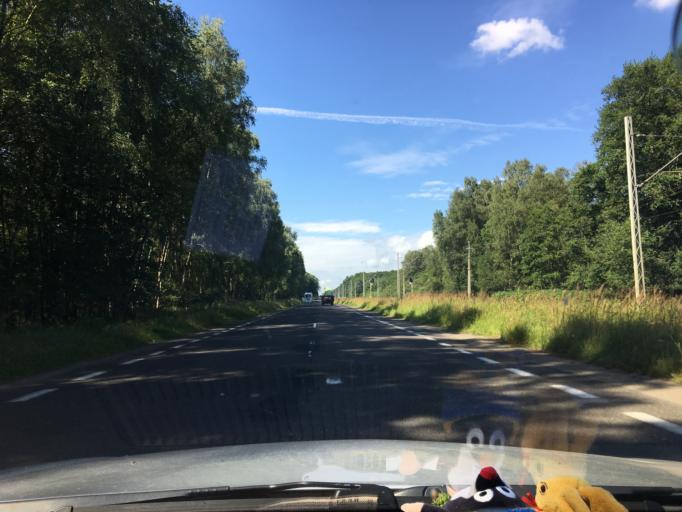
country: PL
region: West Pomeranian Voivodeship
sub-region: Powiat goleniowski
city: Przybiernow
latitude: 53.8449
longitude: 14.7357
